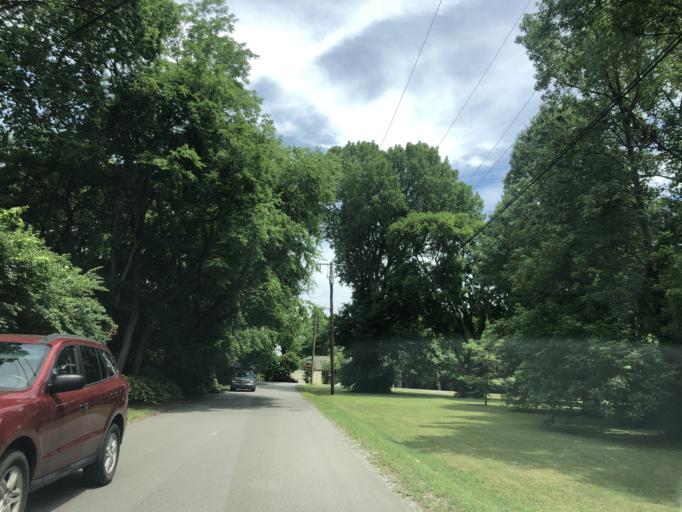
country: US
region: Tennessee
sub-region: Davidson County
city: Oak Hill
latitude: 36.1164
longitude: -86.8027
